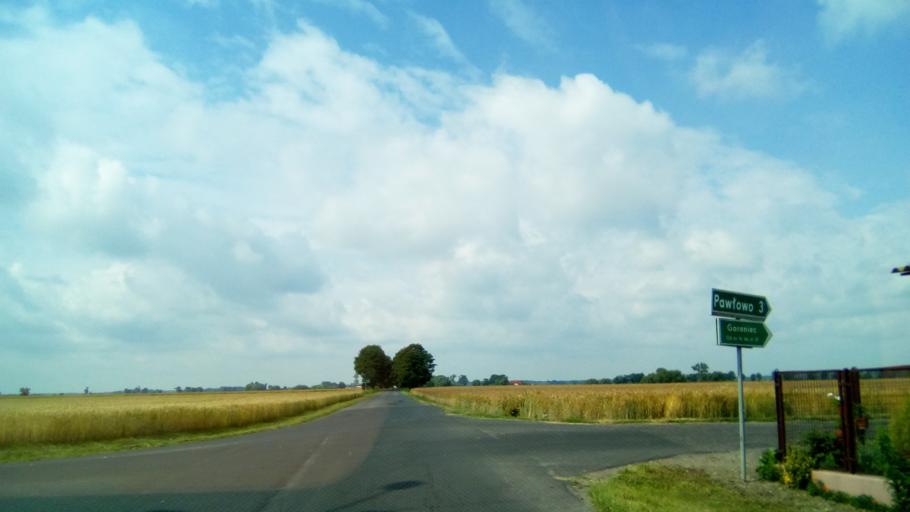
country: PL
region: Greater Poland Voivodeship
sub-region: Powiat gnieznienski
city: Czerniejewo
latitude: 52.4542
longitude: 17.5426
